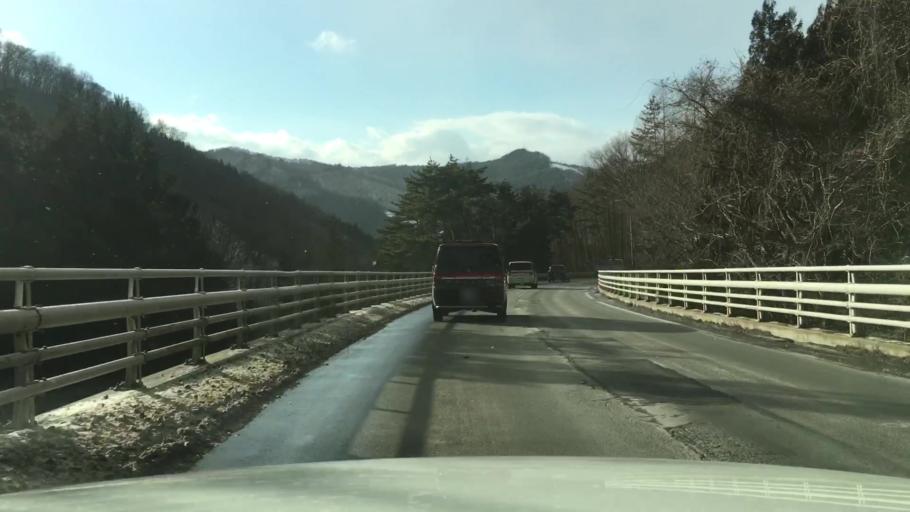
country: JP
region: Iwate
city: Morioka-shi
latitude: 39.6655
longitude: 141.3148
